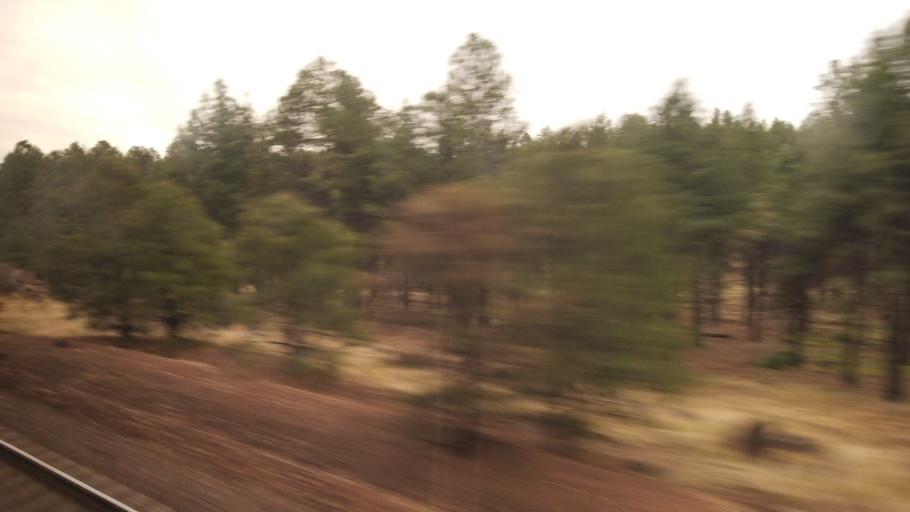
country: US
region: Arizona
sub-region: Coconino County
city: Parks
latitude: 35.2306
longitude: -112.0142
